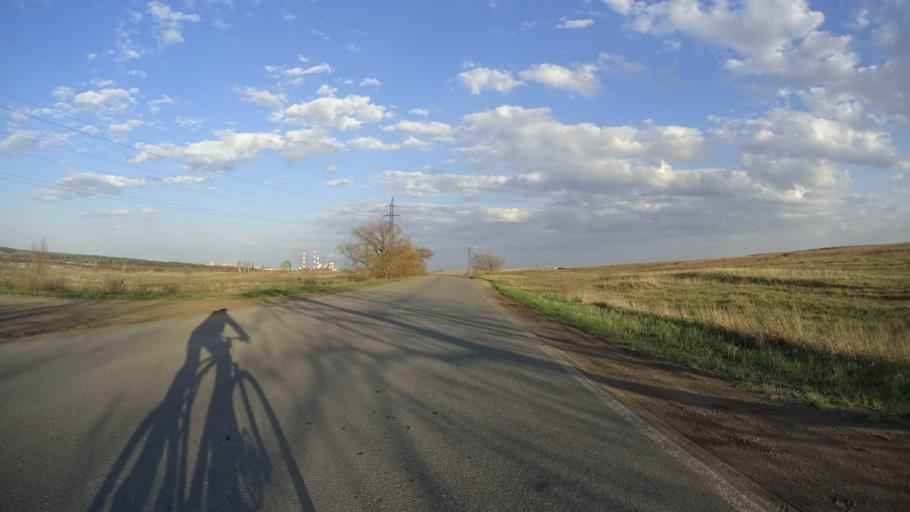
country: RU
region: Chelyabinsk
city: Troitsk
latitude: 54.0536
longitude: 61.5902
